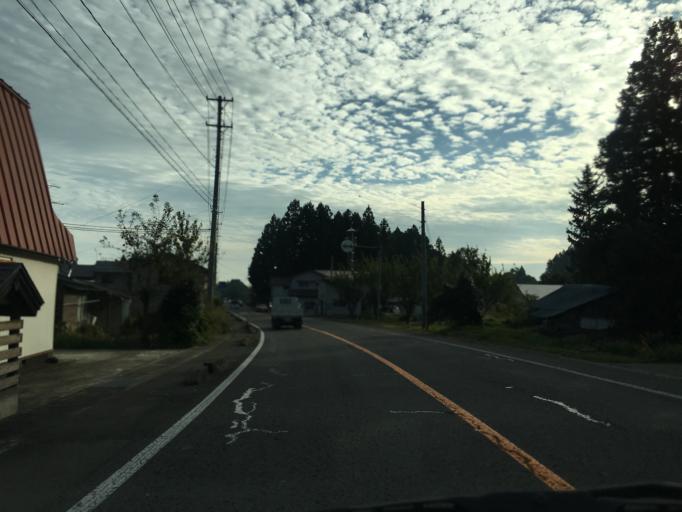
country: JP
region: Fukushima
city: Inawashiro
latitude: 37.5822
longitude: 140.1270
